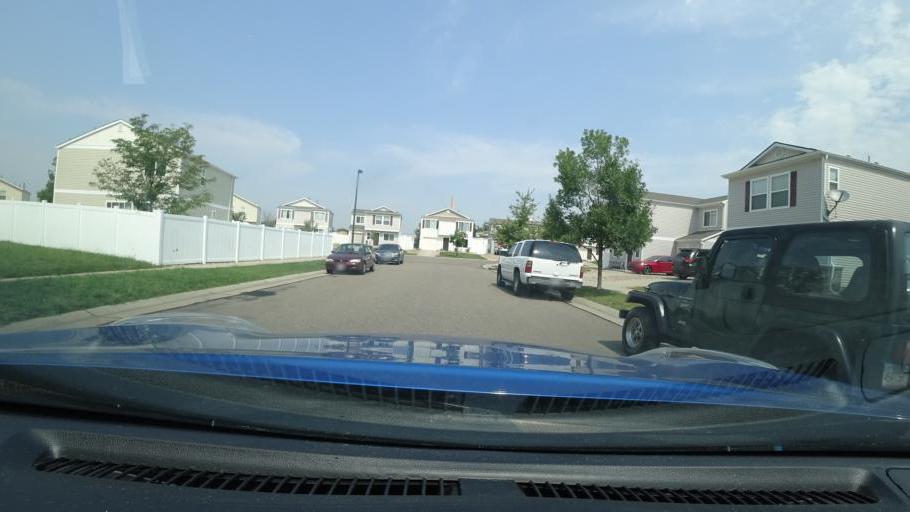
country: US
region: Colorado
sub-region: Adams County
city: Aurora
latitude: 39.7799
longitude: -104.7708
